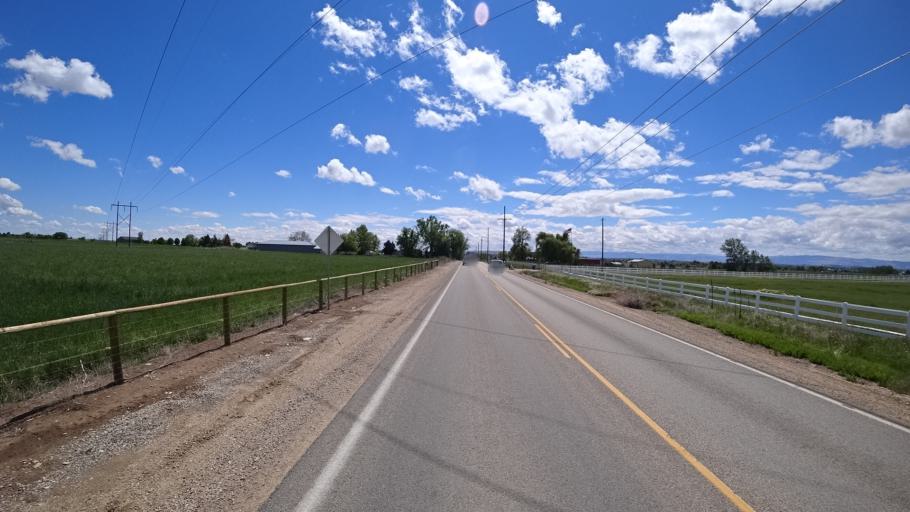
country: US
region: Idaho
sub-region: Ada County
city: Meridian
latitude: 43.5590
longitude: -116.4338
